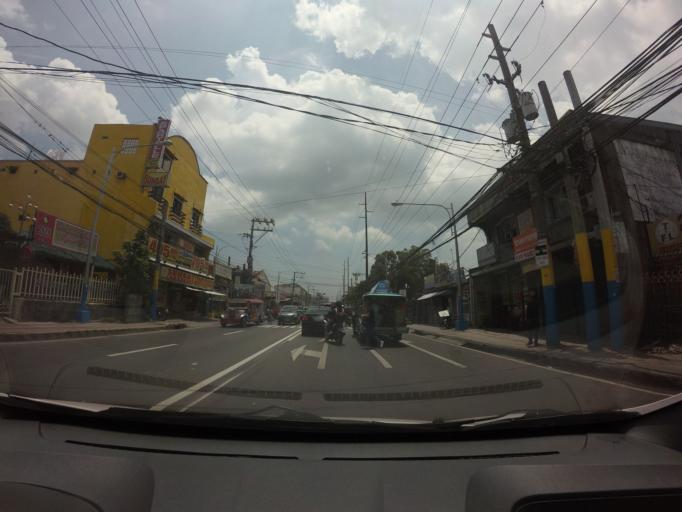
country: PH
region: Calabarzon
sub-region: Province of Laguna
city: San Pedro
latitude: 14.4046
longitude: 121.0470
